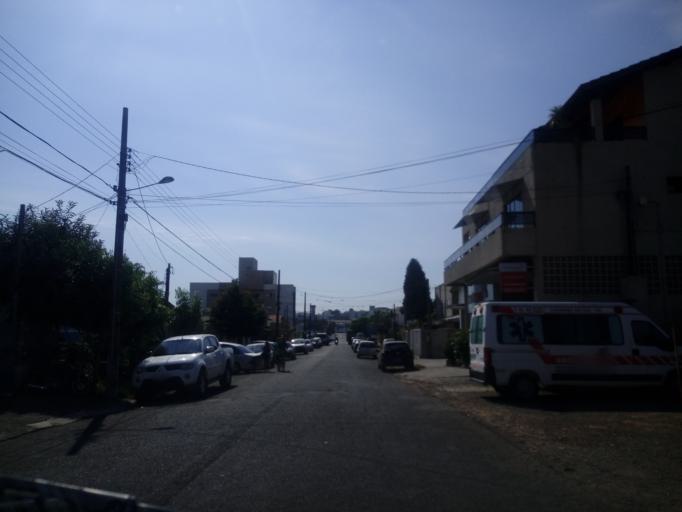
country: BR
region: Santa Catarina
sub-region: Chapeco
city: Chapeco
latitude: -27.0824
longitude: -52.6263
